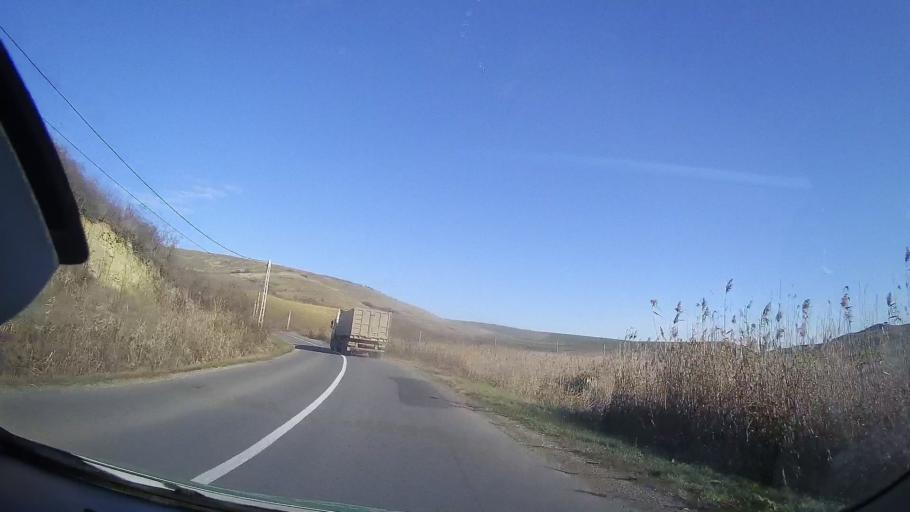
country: RO
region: Mures
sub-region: Comuna Mihesu de Campie
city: Mihesu de Campie
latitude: 46.6490
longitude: 24.1546
